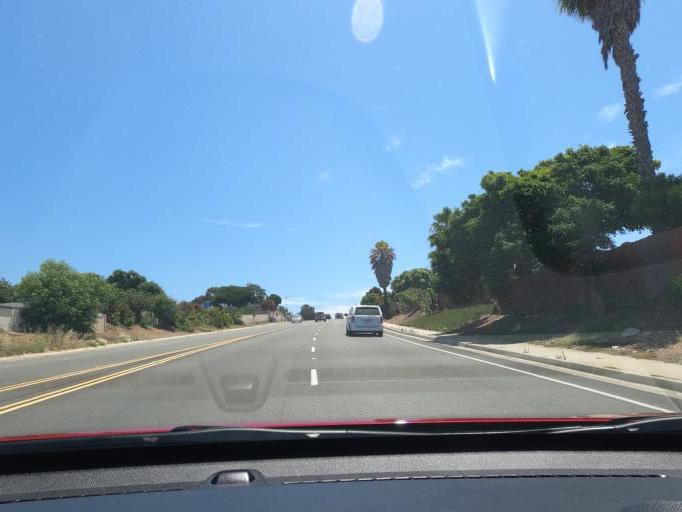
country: US
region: California
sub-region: San Diego County
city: Imperial Beach
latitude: 32.5736
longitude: -117.0516
